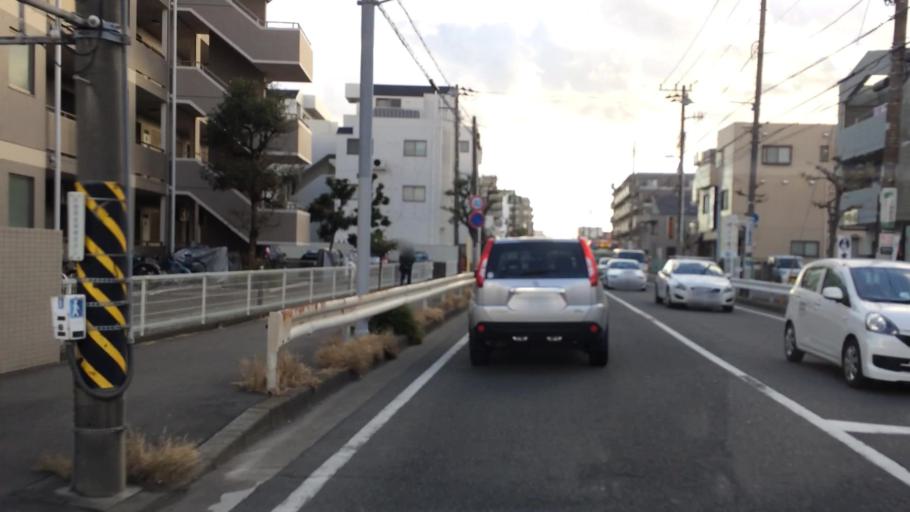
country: JP
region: Kanagawa
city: Fujisawa
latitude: 35.3237
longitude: 139.4658
